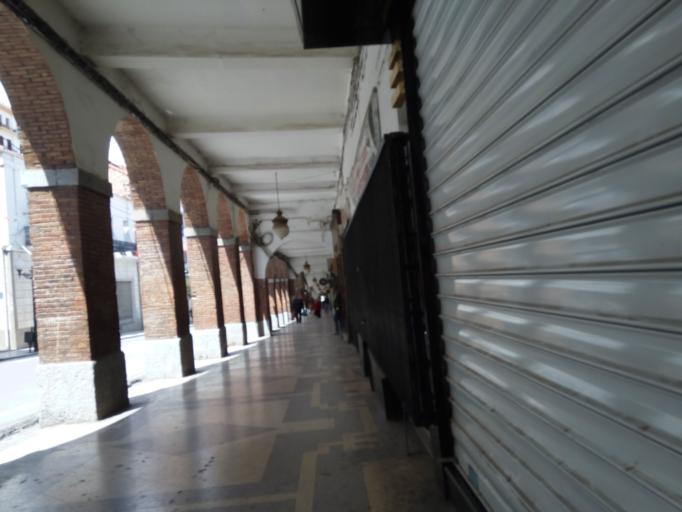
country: DZ
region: Constantine
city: Constantine
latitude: 36.3618
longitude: 6.6076
